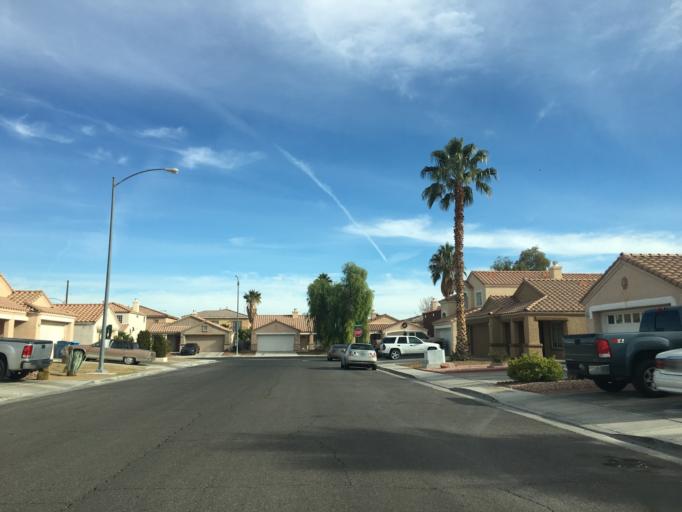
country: US
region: Nevada
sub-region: Clark County
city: Enterprise
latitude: 36.0204
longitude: -115.1657
